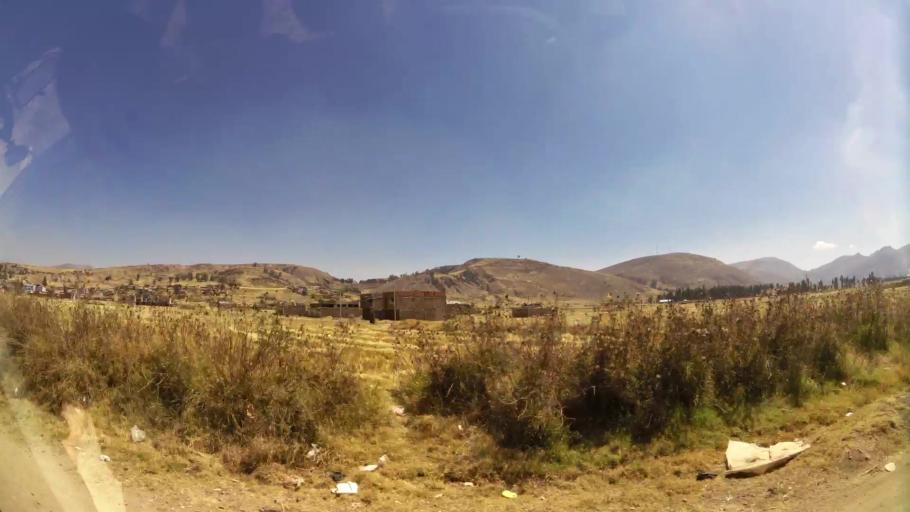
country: PE
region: Junin
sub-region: Provincia de Jauja
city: Jauja
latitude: -11.7647
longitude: -75.4965
